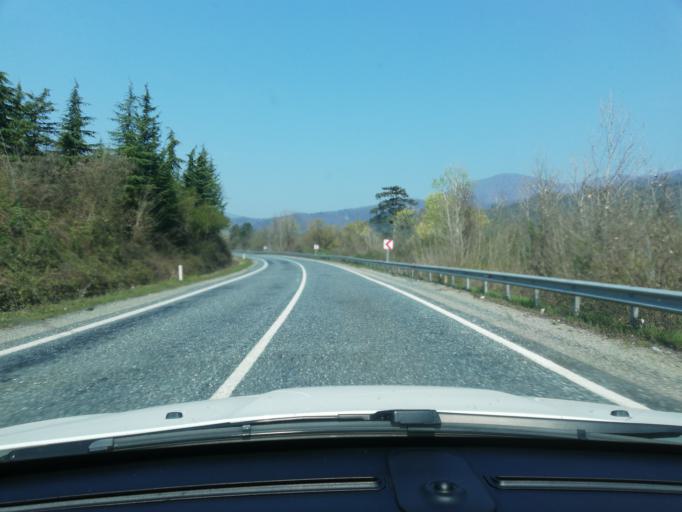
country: TR
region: Zonguldak
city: Gokcebey
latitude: 41.2288
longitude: 32.2105
